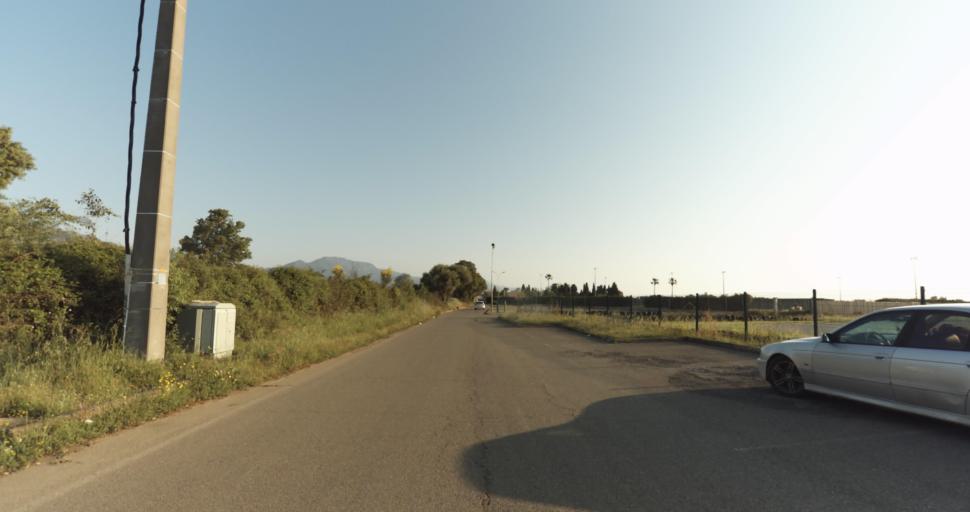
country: FR
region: Corsica
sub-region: Departement de la Haute-Corse
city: Biguglia
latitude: 42.6068
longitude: 9.4440
